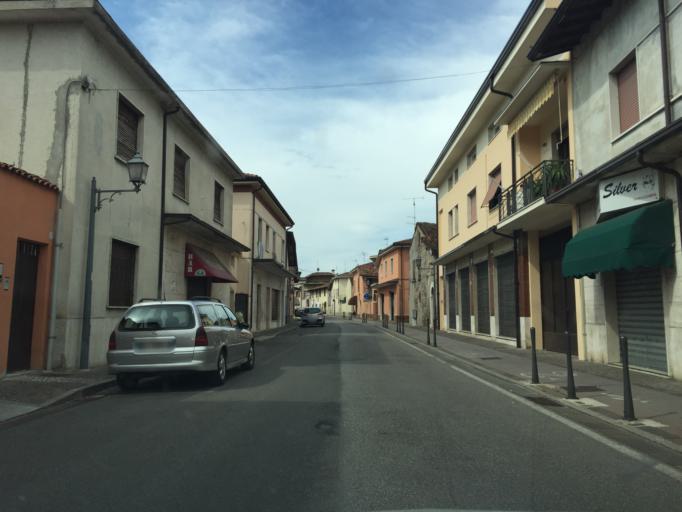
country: IT
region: Lombardy
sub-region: Provincia di Brescia
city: Ghedi
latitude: 45.4042
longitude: 10.2747
